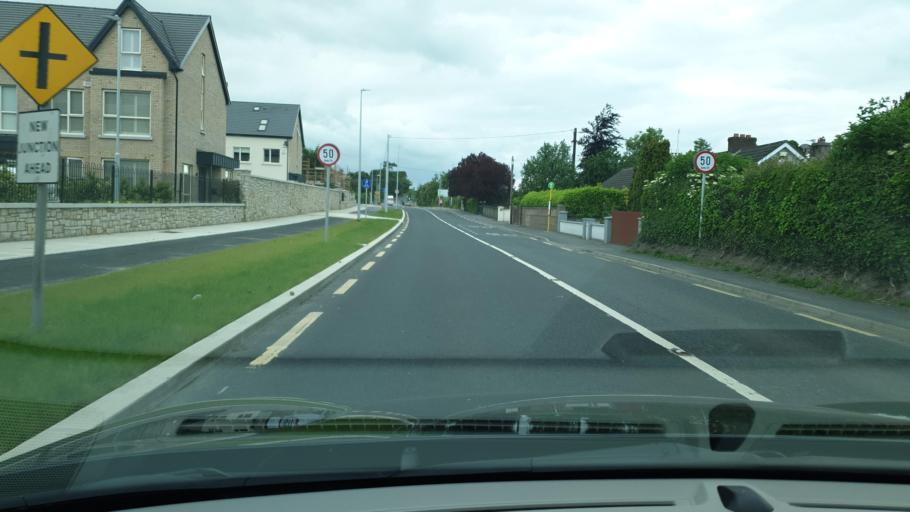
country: IE
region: Leinster
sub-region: An Mhi
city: Dunboyne
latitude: 53.4159
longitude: -6.4590
